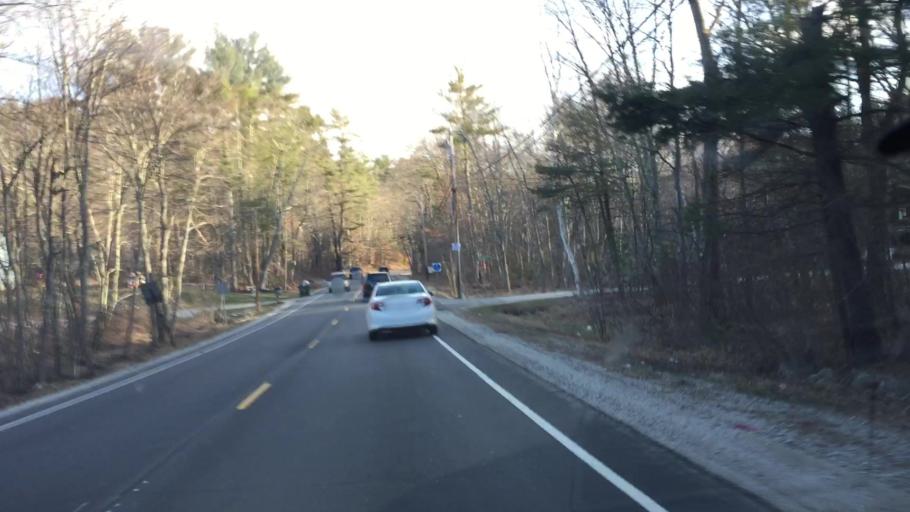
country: US
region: New Hampshire
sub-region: Rockingham County
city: Londonderry
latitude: 42.8293
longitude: -71.3653
